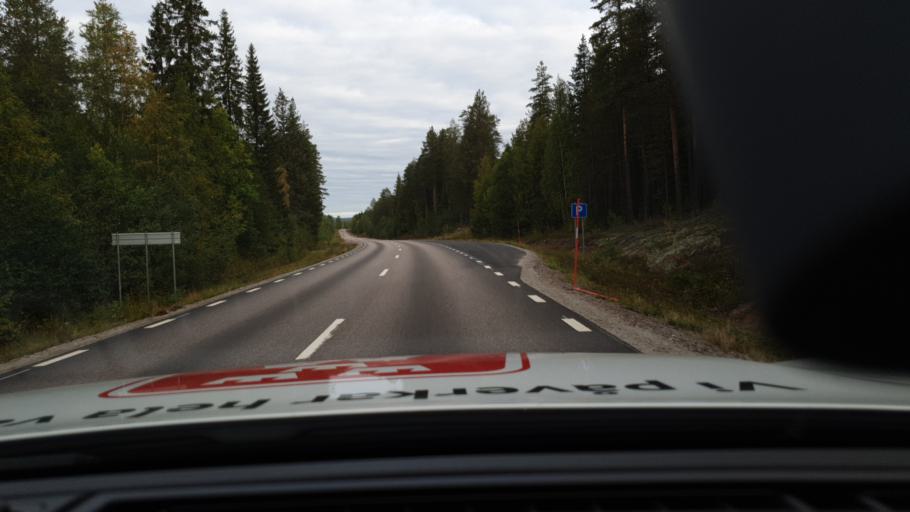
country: SE
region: Norrbotten
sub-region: Overkalix Kommun
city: OEverkalix
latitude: 66.3954
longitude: 22.8173
